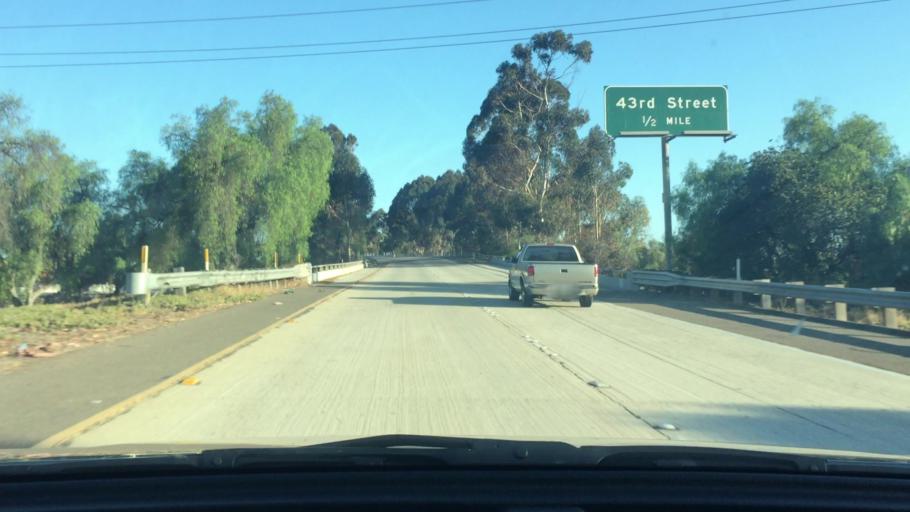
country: US
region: California
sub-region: San Diego County
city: National City
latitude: 32.6872
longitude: -117.0919
